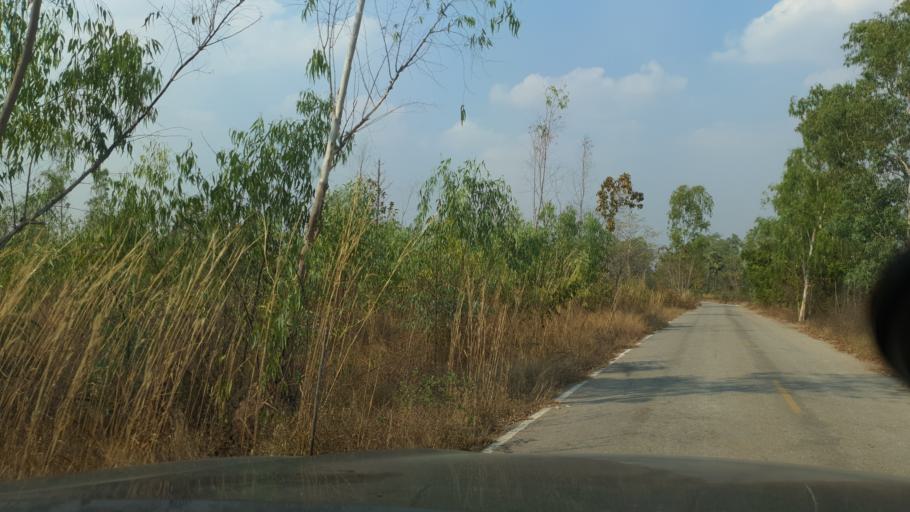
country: TH
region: Sukhothai
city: Ban Dan Lan Hoi
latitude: 17.0069
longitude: 99.5584
